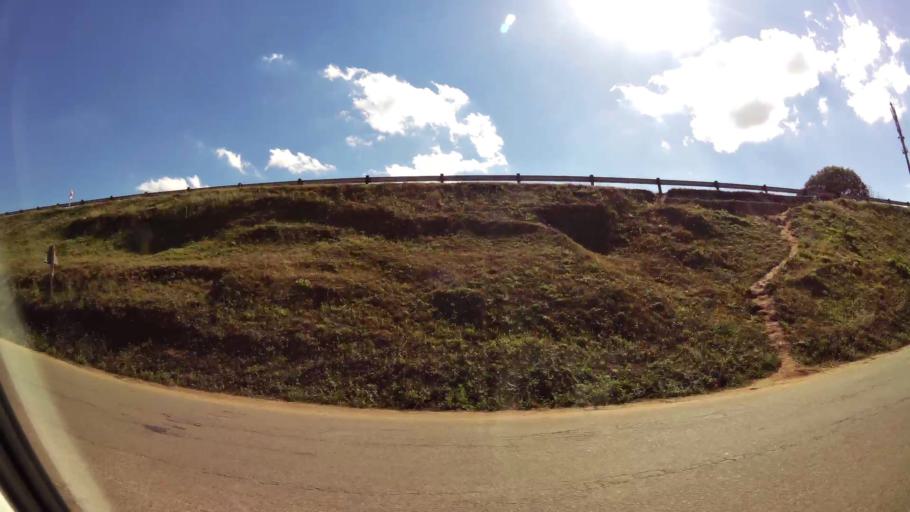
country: ZA
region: Limpopo
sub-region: Mopani District Municipality
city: Tzaneen
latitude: -23.8209
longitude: 30.1635
